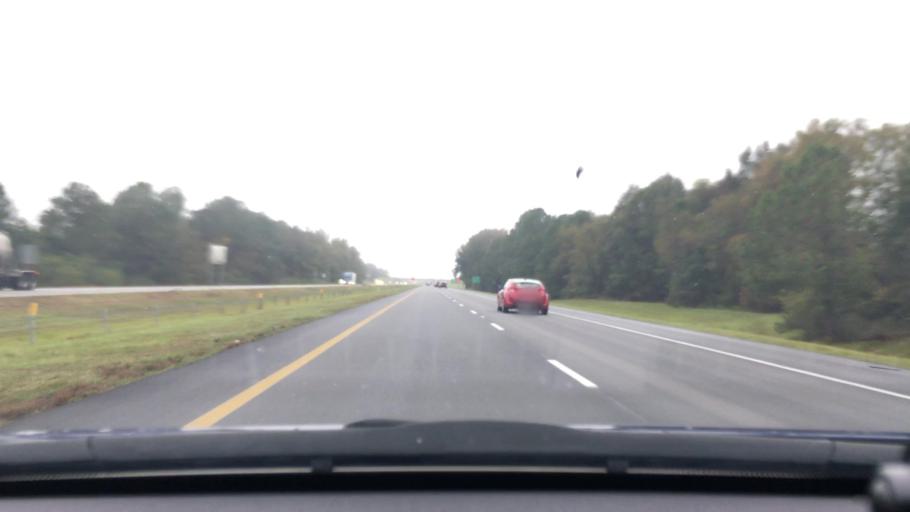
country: US
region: South Carolina
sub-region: Lee County
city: Bishopville
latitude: 34.1874
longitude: -80.1990
